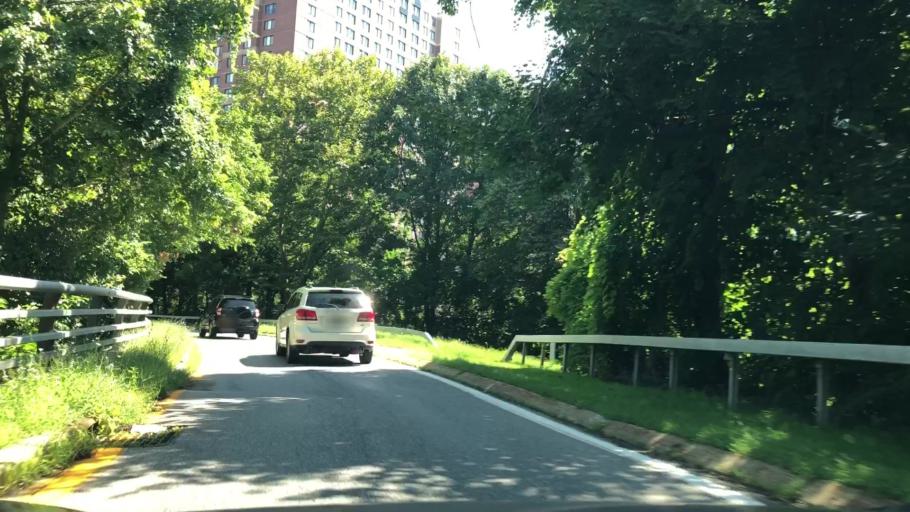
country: US
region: New York
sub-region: Westchester County
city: White Plains
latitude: 41.0301
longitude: -73.7762
